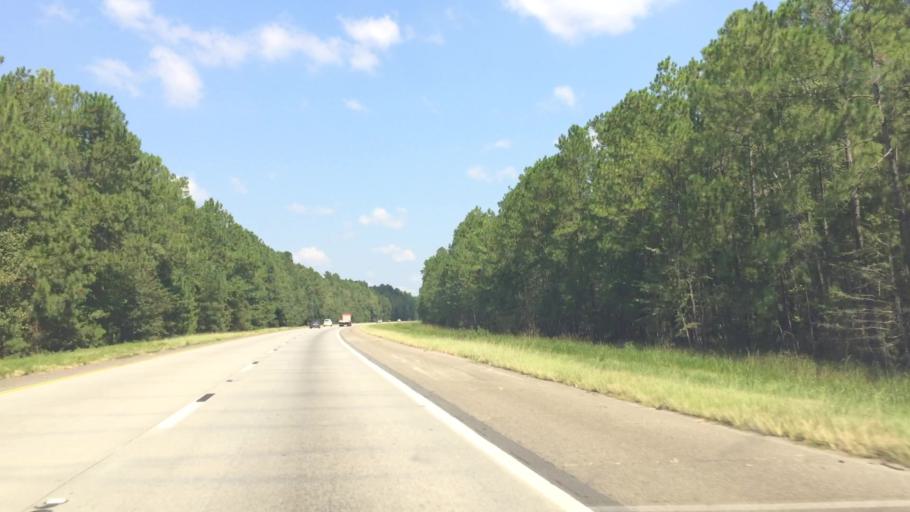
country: US
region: South Carolina
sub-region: Colleton County
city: Walterboro
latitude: 33.0456
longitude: -80.6689
